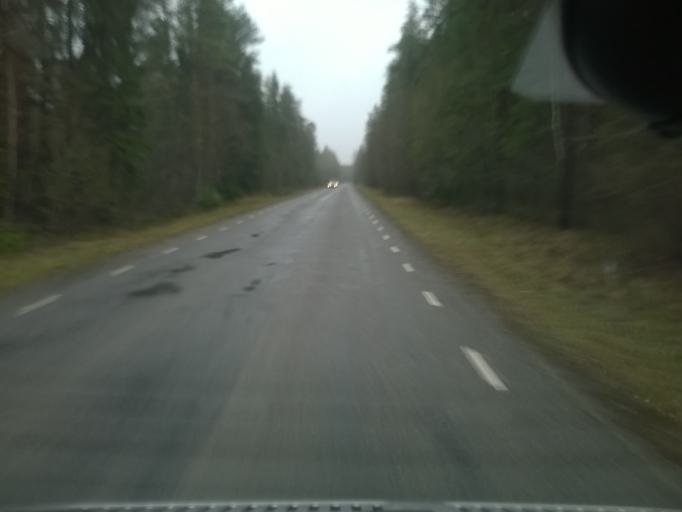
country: EE
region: Raplamaa
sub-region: Kohila vald
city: Kohila
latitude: 59.1891
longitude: 24.6617
